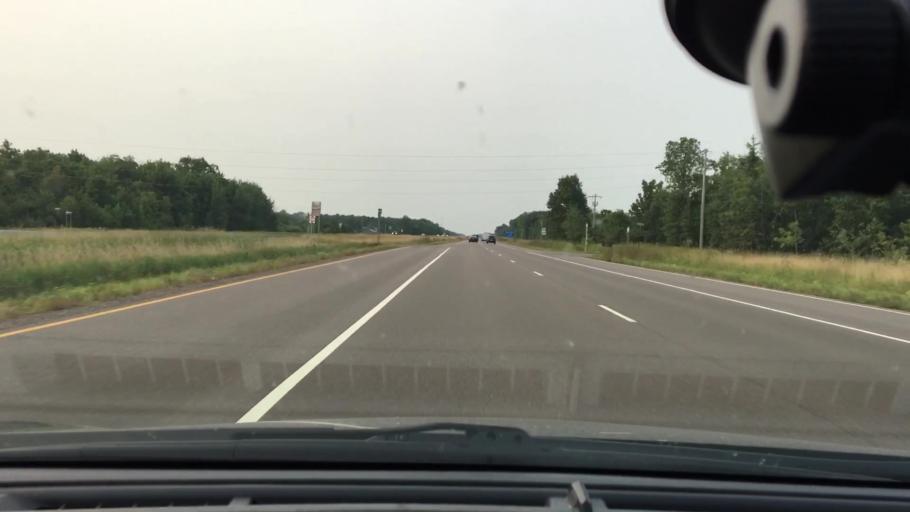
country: US
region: Minnesota
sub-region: Mille Lacs County
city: Milaca
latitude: 45.9072
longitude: -93.6635
